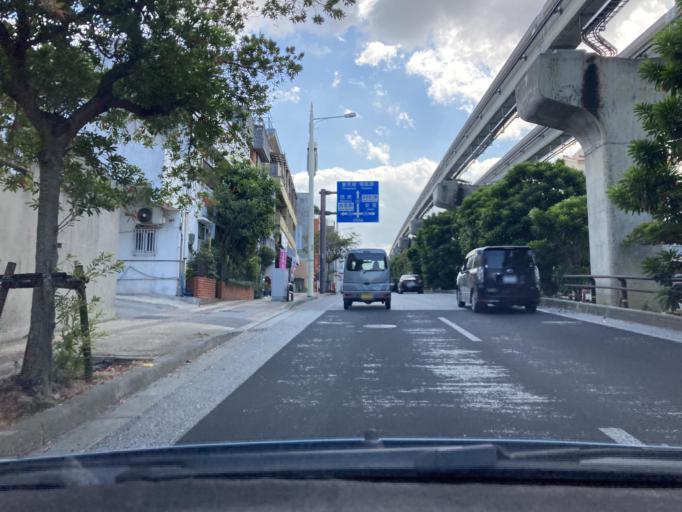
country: JP
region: Okinawa
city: Naha-shi
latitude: 26.2213
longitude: 127.7220
